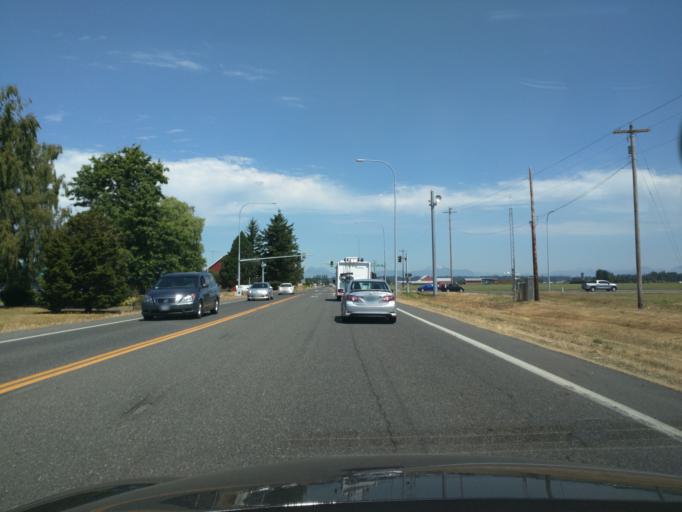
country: US
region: Washington
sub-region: Whatcom County
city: Lynden
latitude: 48.9633
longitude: -122.4851
